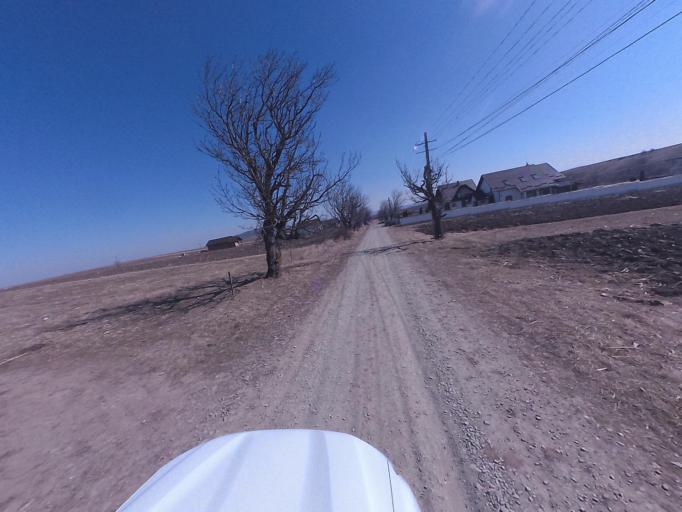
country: RO
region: Neamt
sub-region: Oras Targu Neamt
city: Humulesti
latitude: 47.1864
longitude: 26.3411
